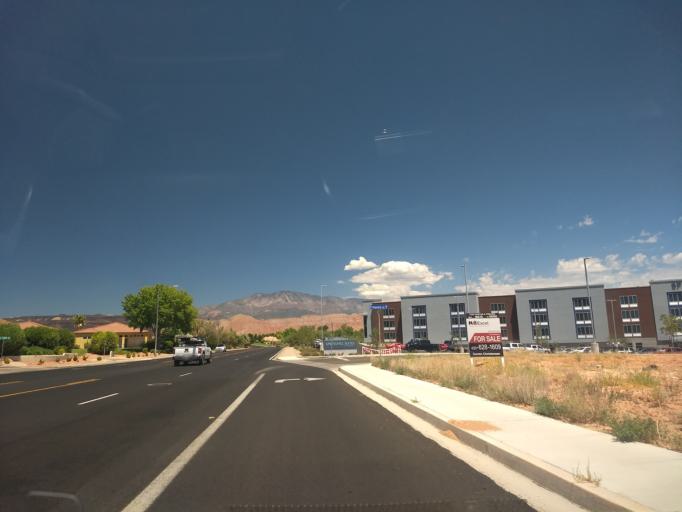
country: US
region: Utah
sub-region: Washington County
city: Washington
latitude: 37.1320
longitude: -113.5268
